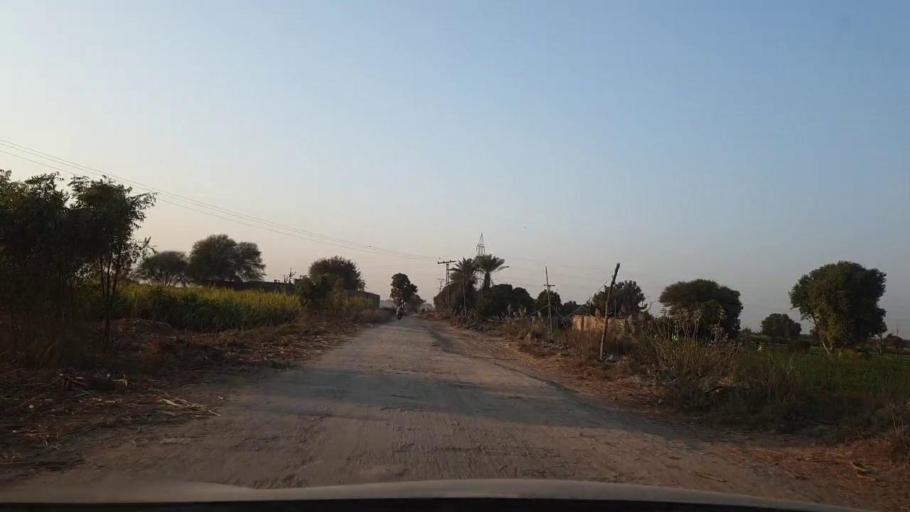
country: PK
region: Sindh
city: Tando Allahyar
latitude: 25.4897
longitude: 68.7468
